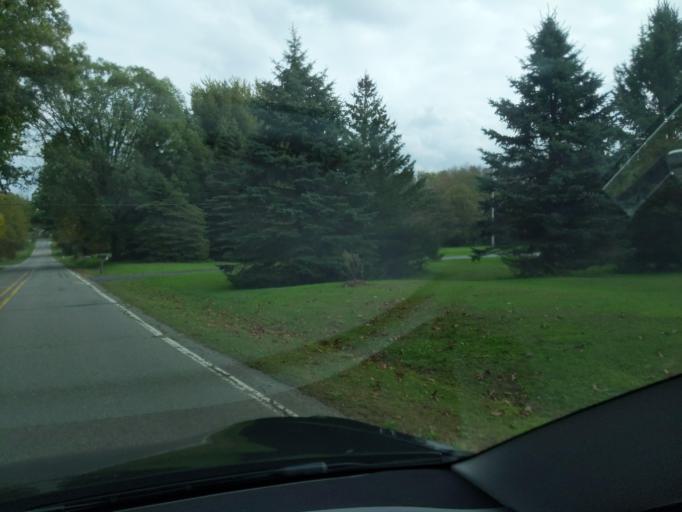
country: US
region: Michigan
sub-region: Ingham County
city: Leslie
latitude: 42.4113
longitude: -84.4002
